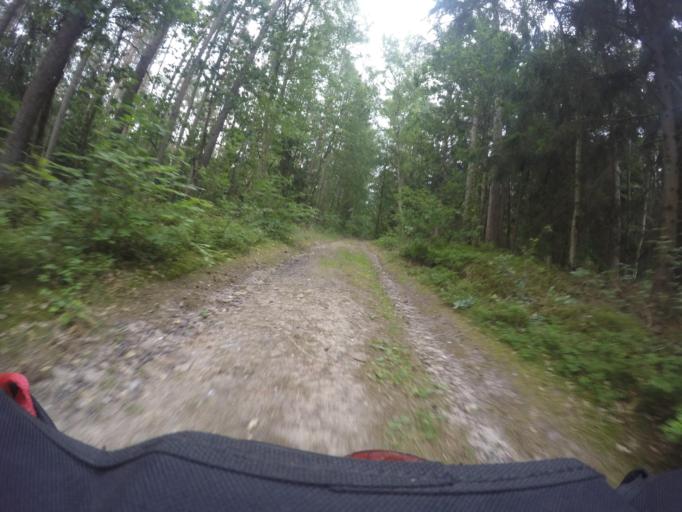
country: DE
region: Lower Saxony
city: Thomasburg
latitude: 53.2171
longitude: 10.6797
